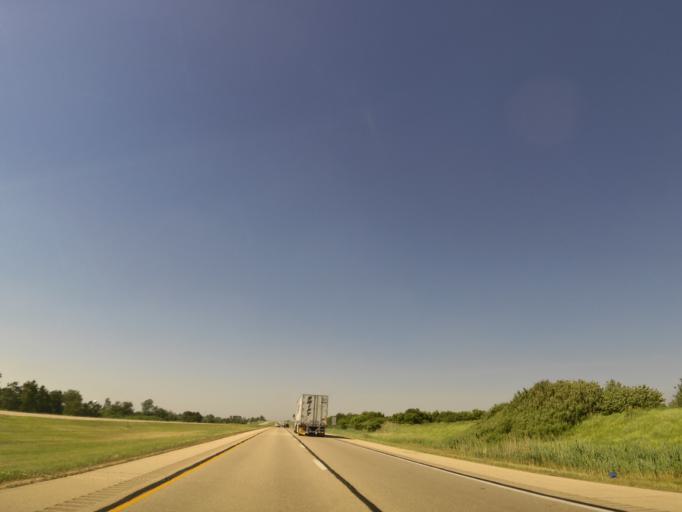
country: US
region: Illinois
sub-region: Ogle County
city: Rochelle
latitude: 41.8591
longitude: -89.0099
